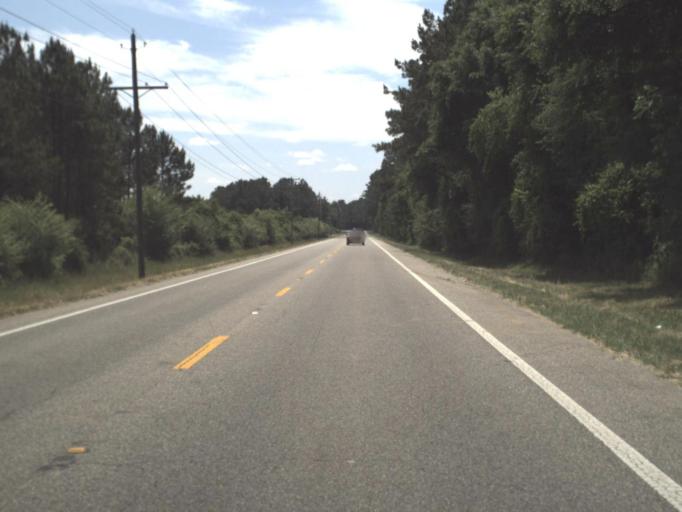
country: US
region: Florida
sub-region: Calhoun County
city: Blountstown
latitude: 30.5386
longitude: -85.1315
